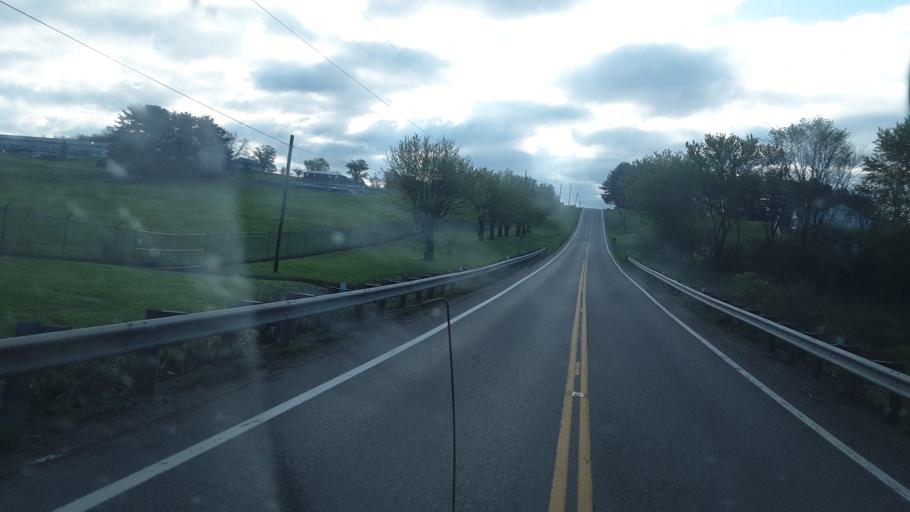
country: US
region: Ohio
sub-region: Muskingum County
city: New Concord
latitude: 39.9368
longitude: -81.6876
